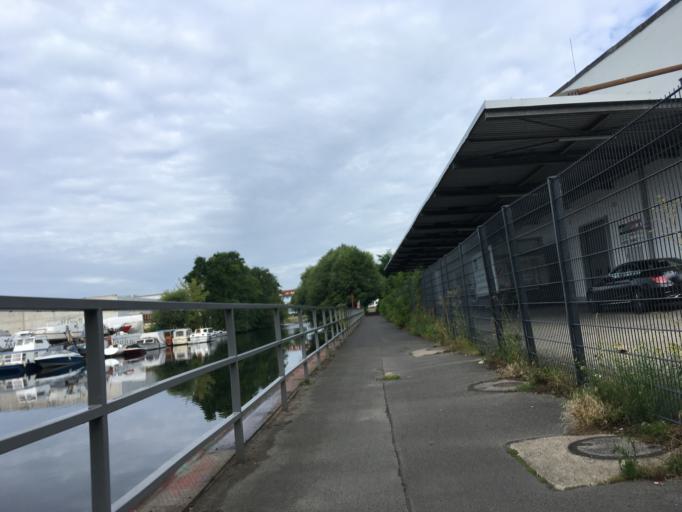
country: DE
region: Berlin
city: Hakenfelde
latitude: 52.5625
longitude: 13.2192
